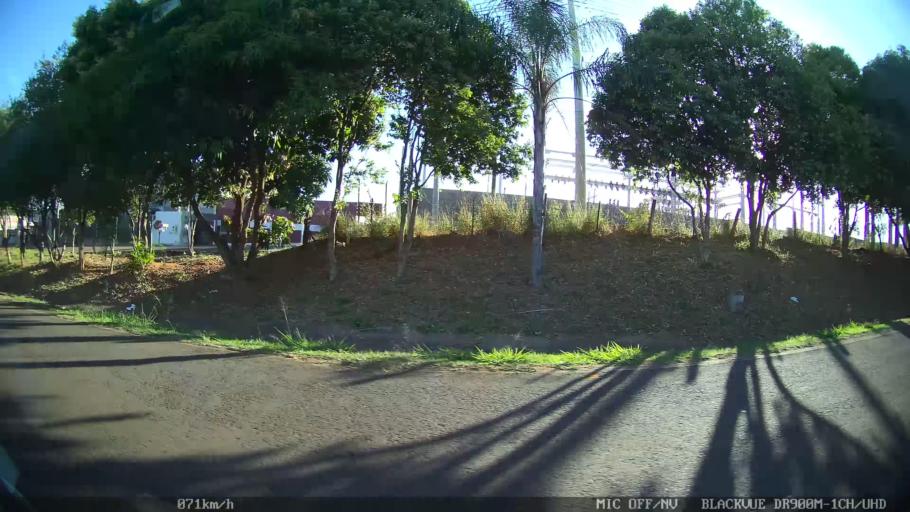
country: BR
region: Sao Paulo
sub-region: Guapiacu
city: Guapiacu
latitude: -20.7852
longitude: -49.2238
